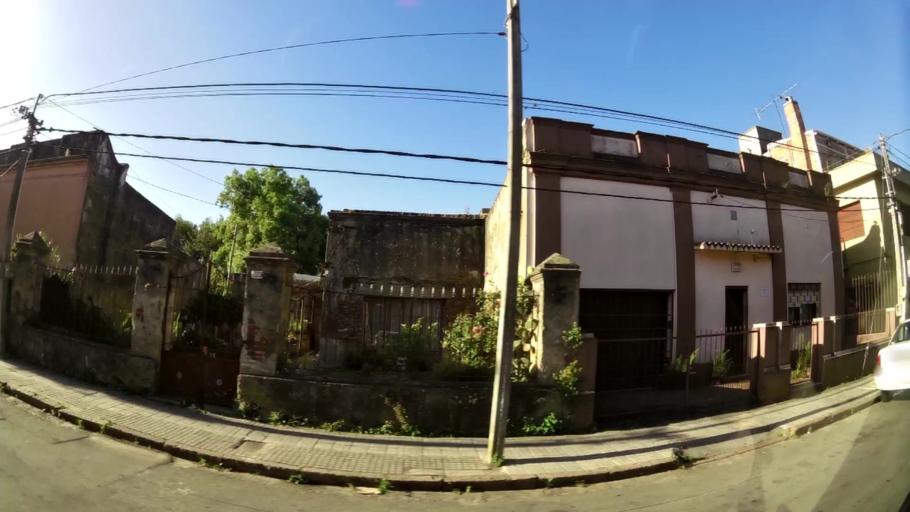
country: UY
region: Canelones
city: La Paz
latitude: -34.8264
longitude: -56.2055
